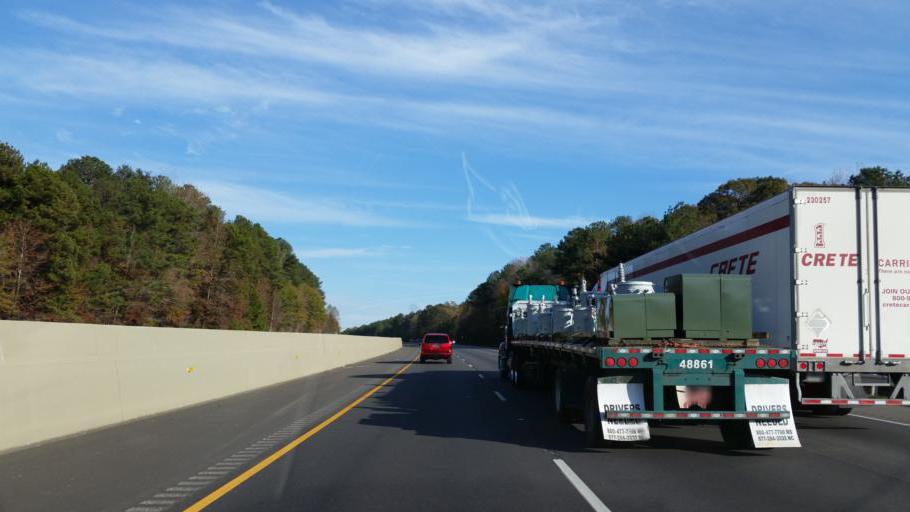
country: US
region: Alabama
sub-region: Tuscaloosa County
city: Coaling
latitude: 33.1713
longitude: -87.4249
